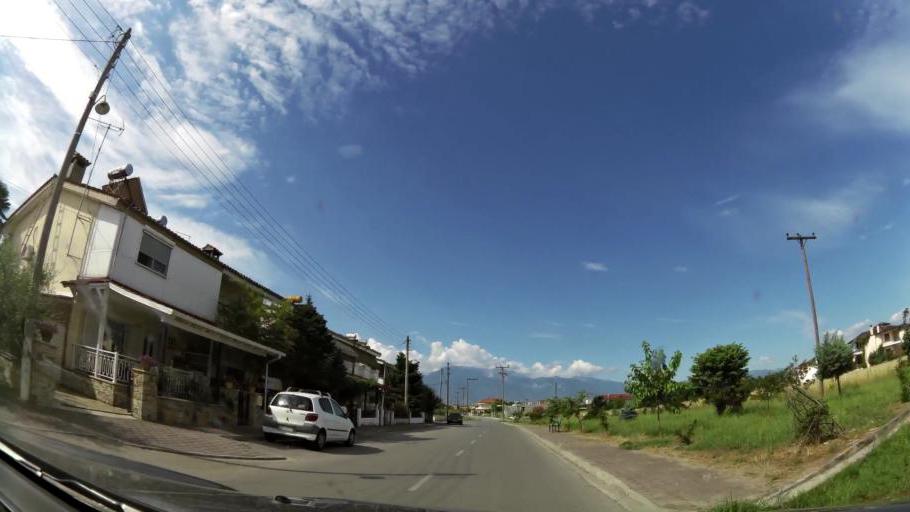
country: GR
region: Central Macedonia
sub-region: Nomos Pierias
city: Katerini
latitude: 40.2832
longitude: 22.5147
